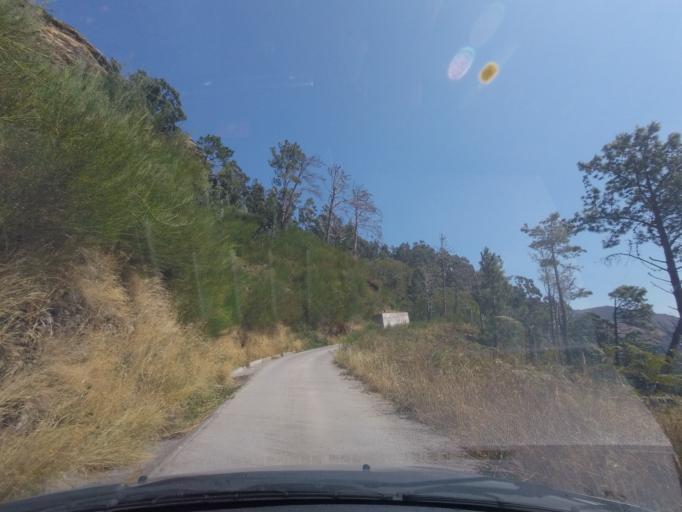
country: PT
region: Madeira
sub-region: Sao Vicente
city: Sao Vicente
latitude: 32.7421
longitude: -17.0292
